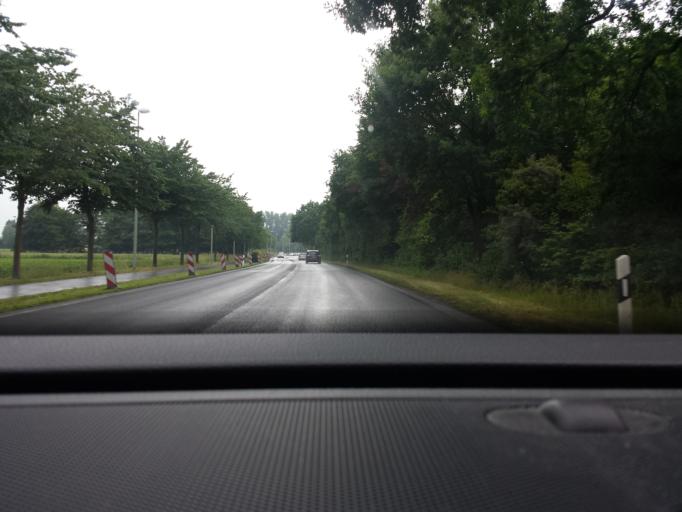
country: DE
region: North Rhine-Westphalia
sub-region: Regierungsbezirk Munster
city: Ahaus
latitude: 52.0672
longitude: 7.0132
